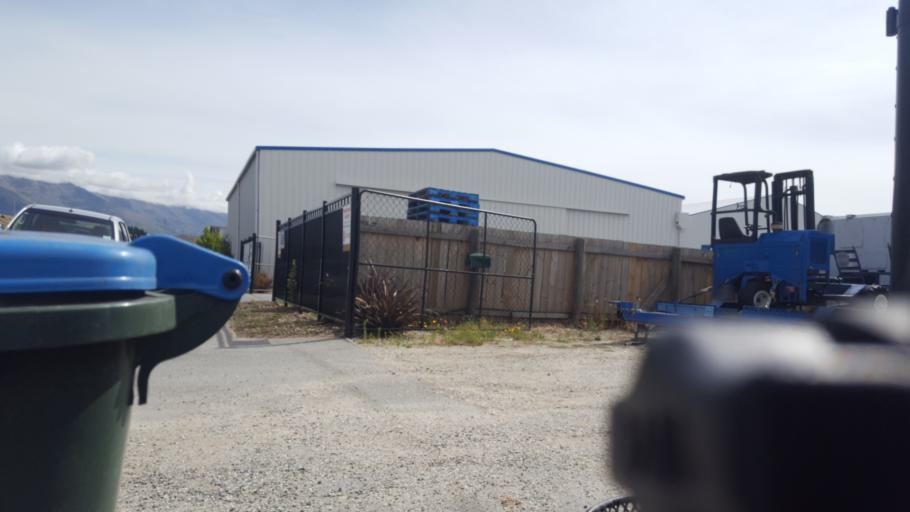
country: NZ
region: Otago
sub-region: Queenstown-Lakes District
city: Wanaka
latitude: -45.0512
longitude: 169.1894
